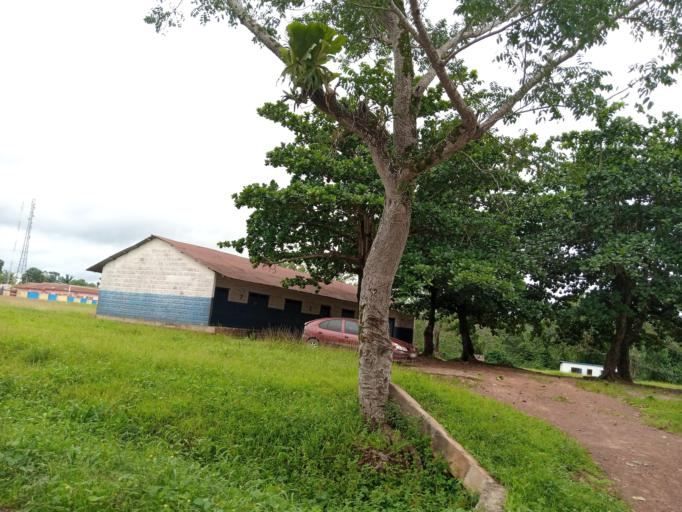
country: SL
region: Southern Province
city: Largo
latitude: 8.2023
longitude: -12.0618
